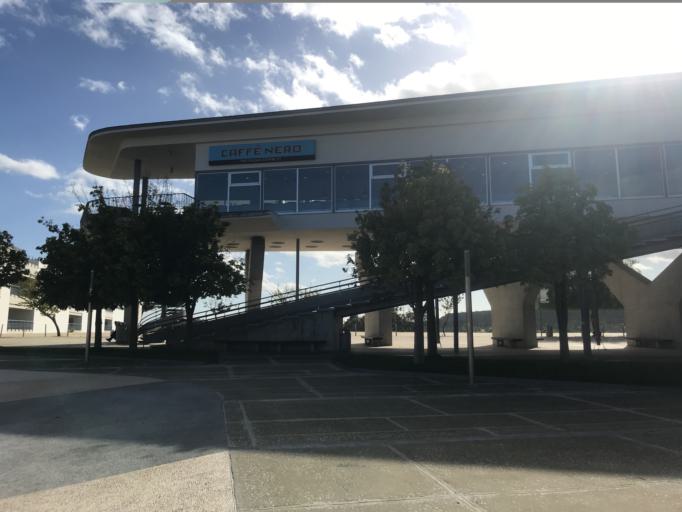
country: CY
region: Lefkosia
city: Geri
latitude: 35.1451
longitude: 33.4093
